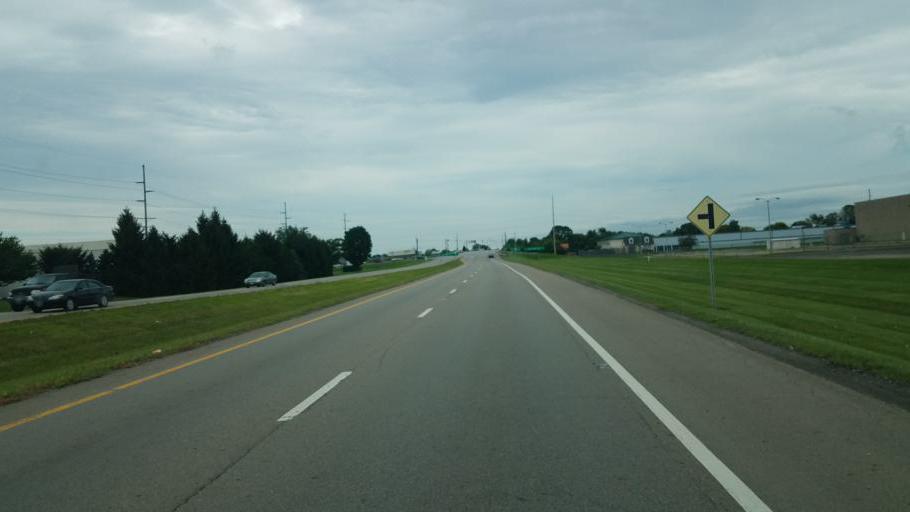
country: US
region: Ohio
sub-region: Franklin County
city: Groveport
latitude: 39.8843
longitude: -82.8832
